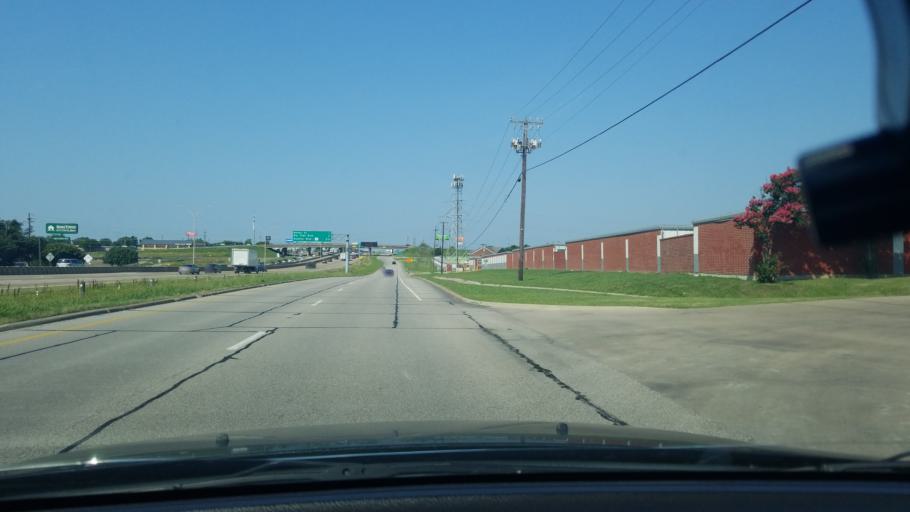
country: US
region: Texas
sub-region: Dallas County
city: Mesquite
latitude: 32.8203
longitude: -96.6351
